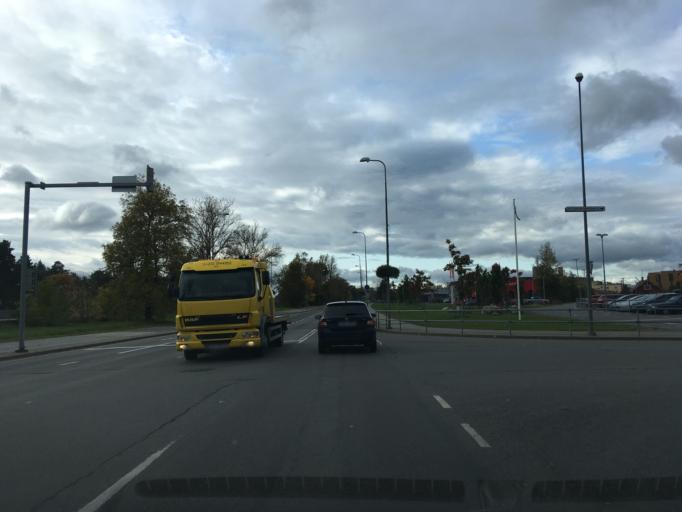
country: EE
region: Harju
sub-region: Saue vald
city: Laagri
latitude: 59.3834
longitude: 24.6701
